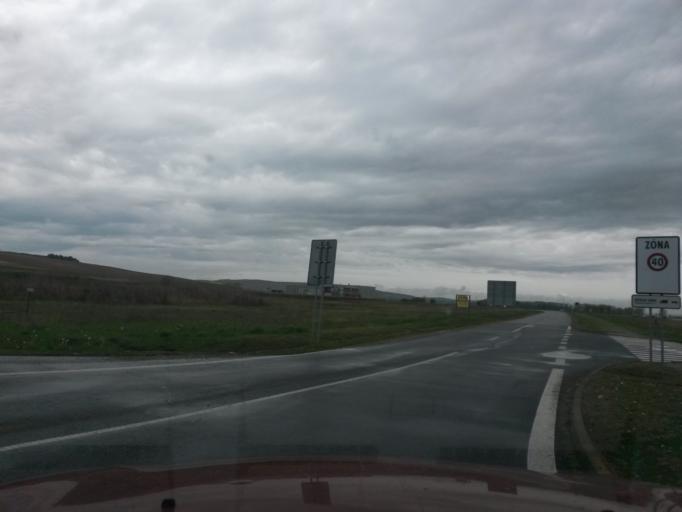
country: HU
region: Borsod-Abauj-Zemplen
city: Gonc
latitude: 48.5486
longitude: 21.2314
